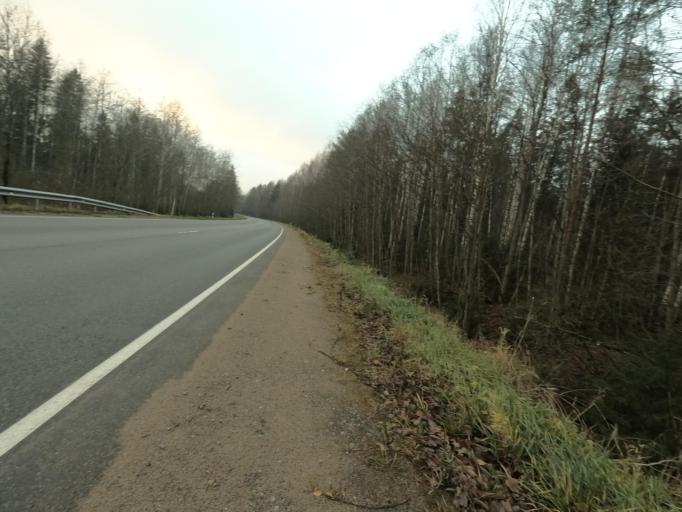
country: RU
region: Leningrad
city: Pavlovo
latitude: 59.8064
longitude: 30.9609
